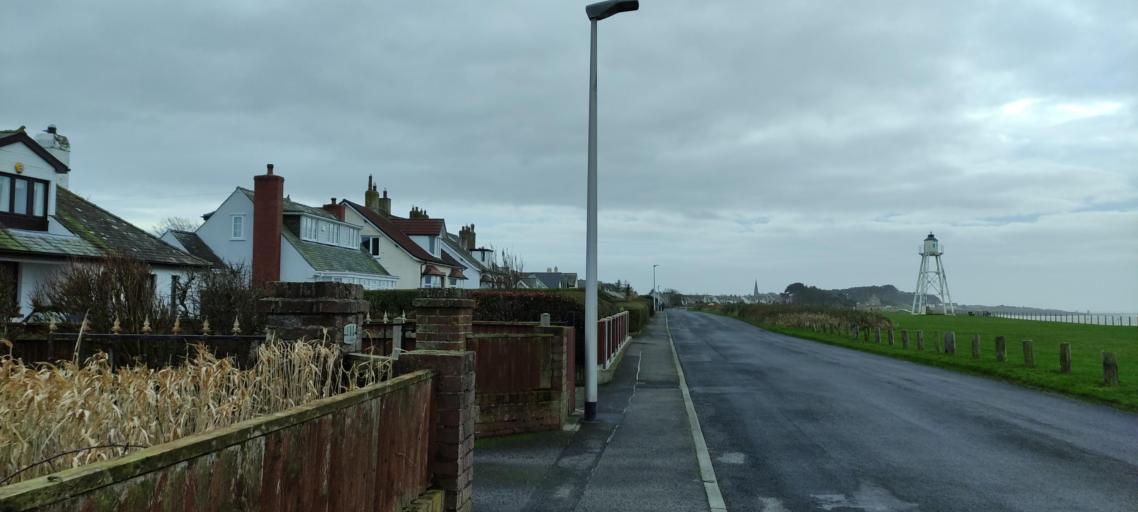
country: GB
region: England
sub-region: Cumbria
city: Silloth
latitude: 54.8807
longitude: -3.3796
